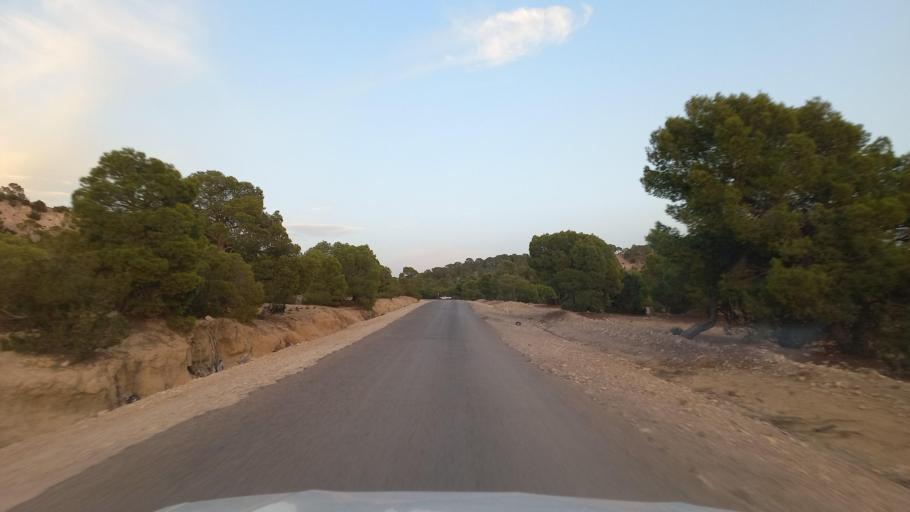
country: TN
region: Al Qasrayn
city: Sbiba
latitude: 35.4110
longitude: 8.9597
